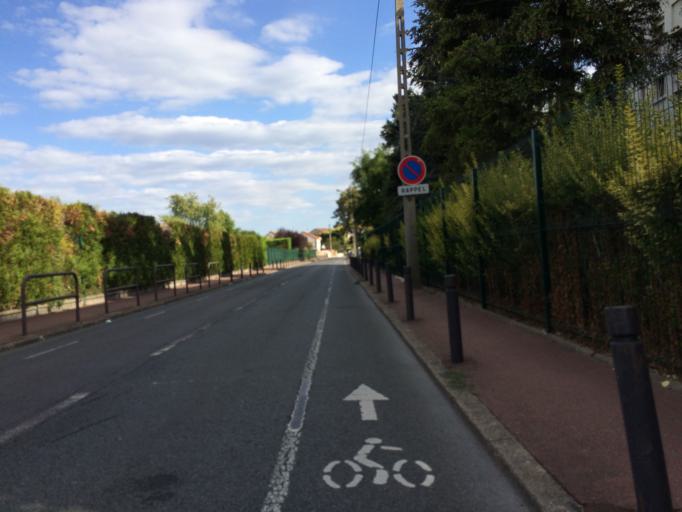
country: FR
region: Ile-de-France
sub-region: Departement de l'Essonne
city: Chilly-Mazarin
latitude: 48.7081
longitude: 2.3210
